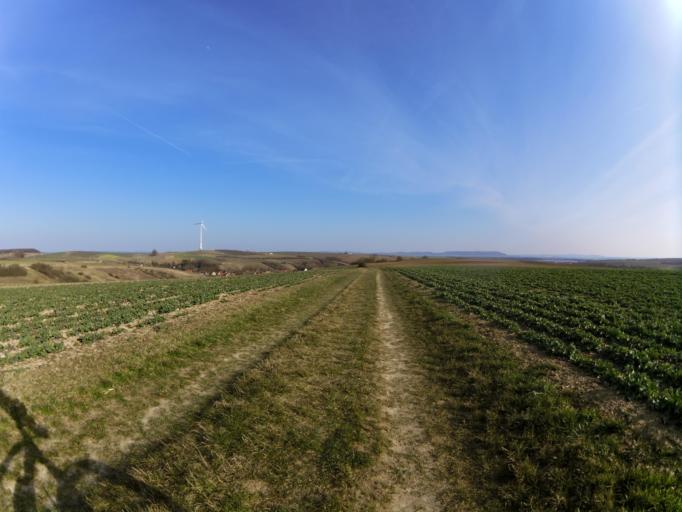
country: DE
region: Bavaria
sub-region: Regierungsbezirk Unterfranken
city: Prosselsheim
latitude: 49.8320
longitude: 10.1387
